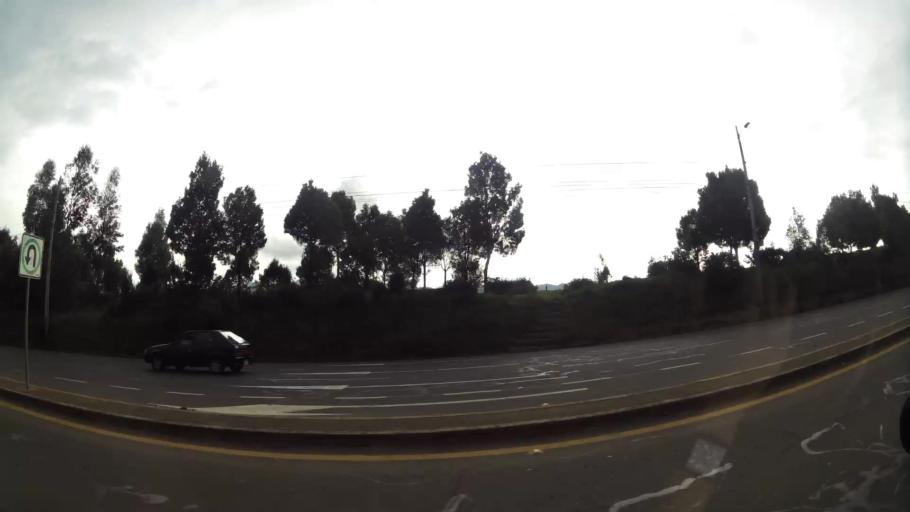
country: EC
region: Pichincha
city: Sangolqui
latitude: -0.3168
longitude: -78.5217
